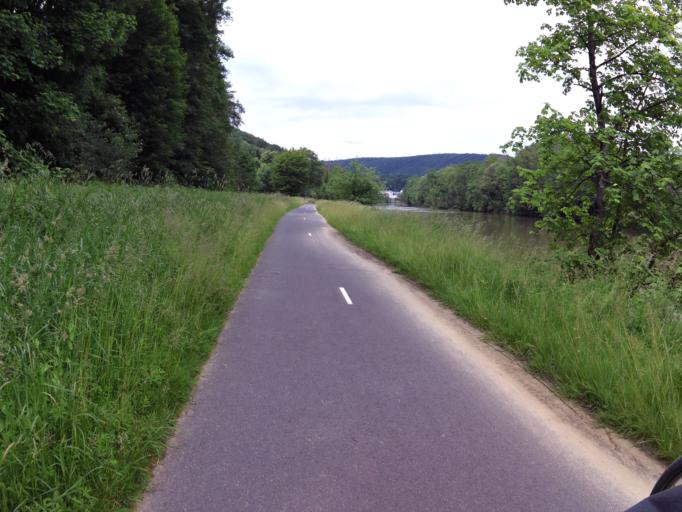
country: FR
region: Champagne-Ardenne
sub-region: Departement des Ardennes
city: Nouzonville
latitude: 49.8057
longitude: 4.7461
